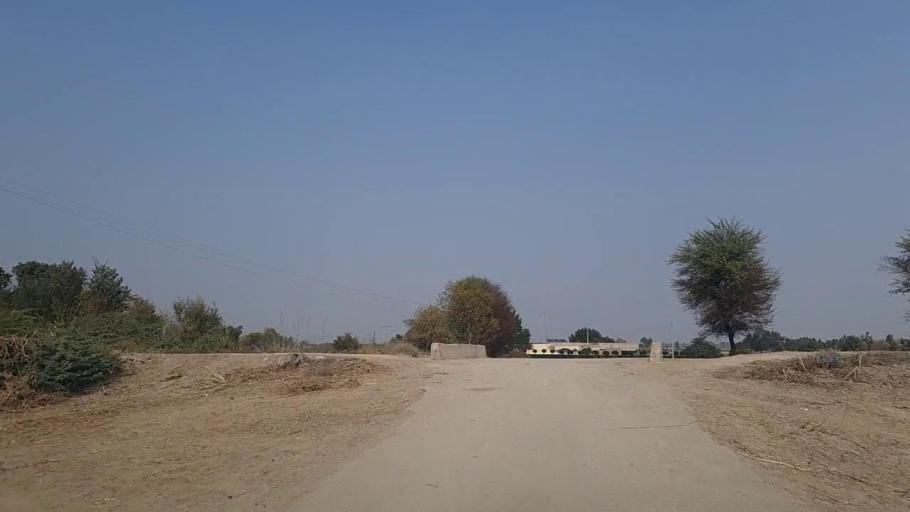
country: PK
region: Sindh
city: Daur
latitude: 26.4693
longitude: 68.5118
